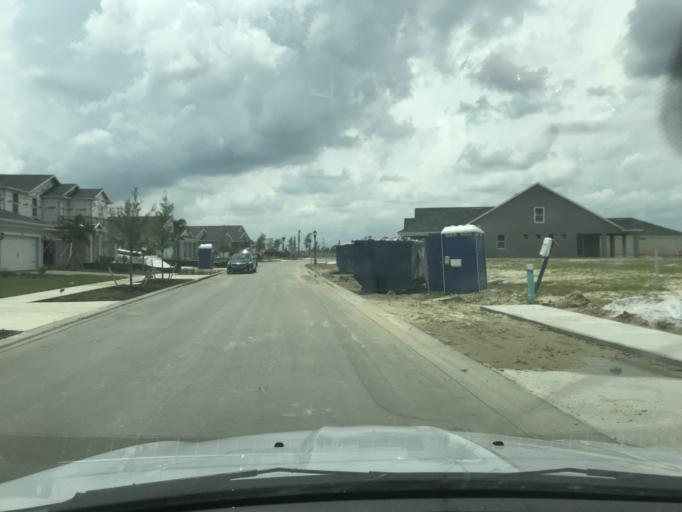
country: US
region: Florida
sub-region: Lee County
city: Olga
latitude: 26.7804
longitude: -81.7435
